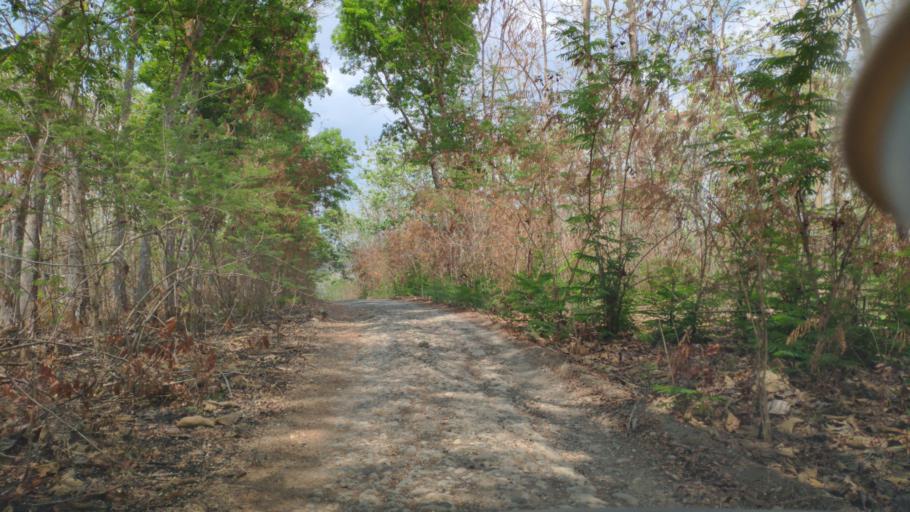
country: ID
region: Central Java
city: Singonegoro
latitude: -6.9897
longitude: 111.5423
